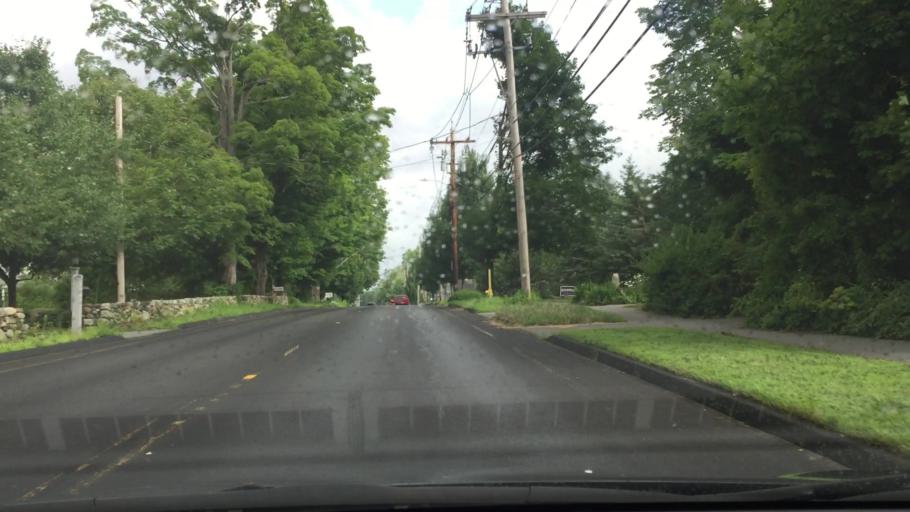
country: US
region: Massachusetts
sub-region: Middlesex County
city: Littleton Common
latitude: 42.5412
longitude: -71.4701
